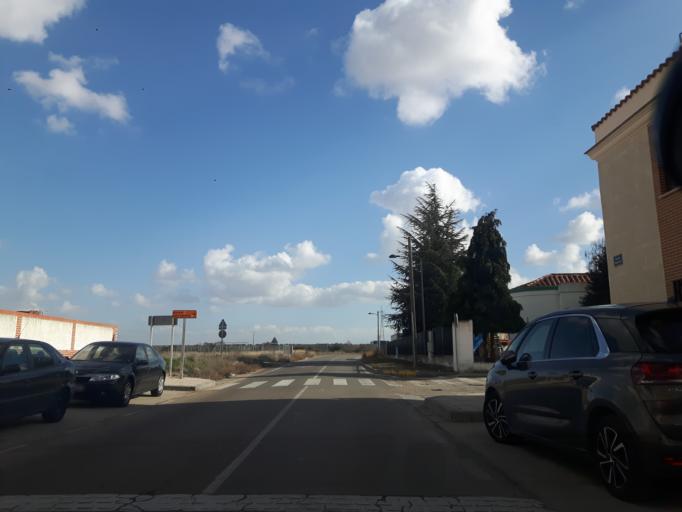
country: ES
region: Castille and Leon
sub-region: Provincia de Salamanca
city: Castellanos de Moriscos
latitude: 41.0176
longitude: -5.5896
